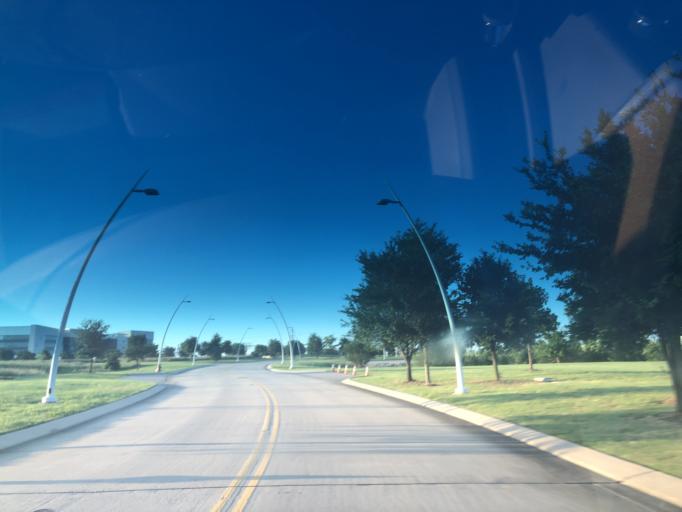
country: US
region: Texas
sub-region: Dallas County
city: Grand Prairie
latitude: 32.7033
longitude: -97.0268
